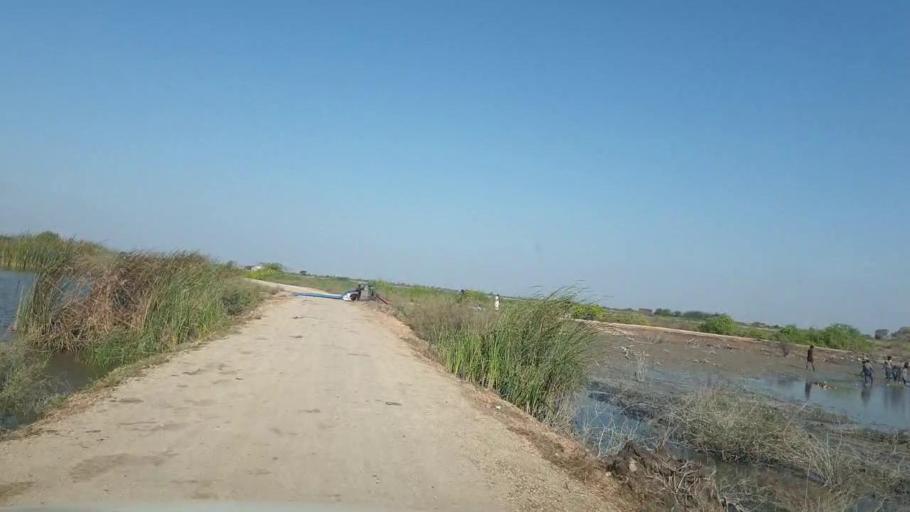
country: PK
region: Sindh
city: Chuhar Jamali
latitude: 24.4638
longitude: 67.8656
